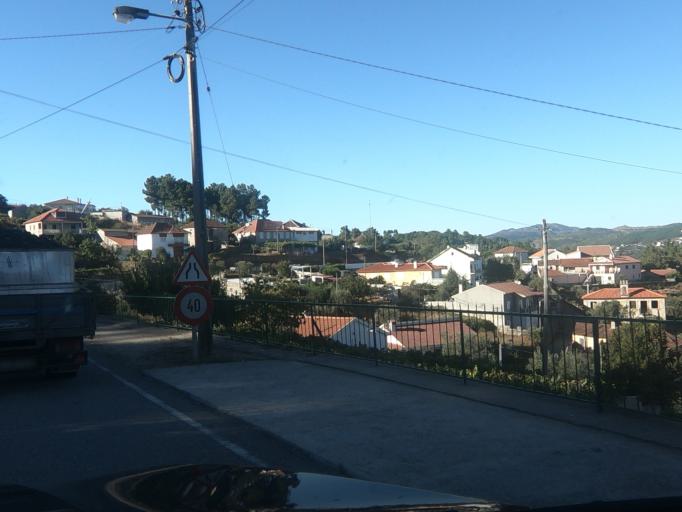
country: PT
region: Vila Real
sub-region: Sabrosa
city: Sabrosa
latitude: 41.2935
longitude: -7.5786
